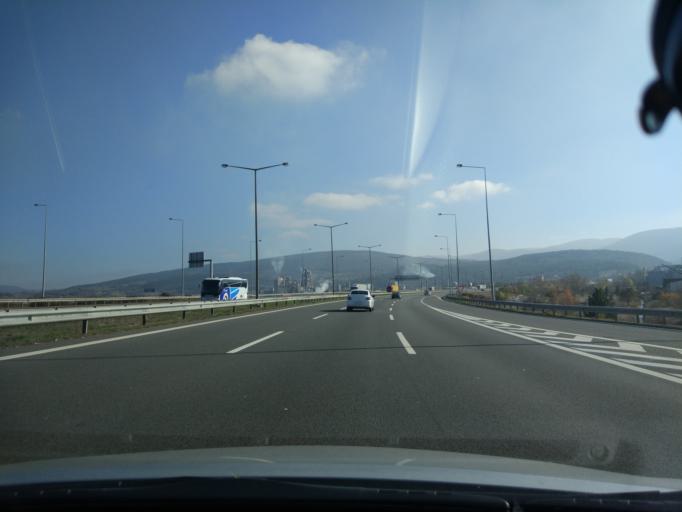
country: TR
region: Bolu
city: Bolu
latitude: 40.7602
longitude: 31.7669
